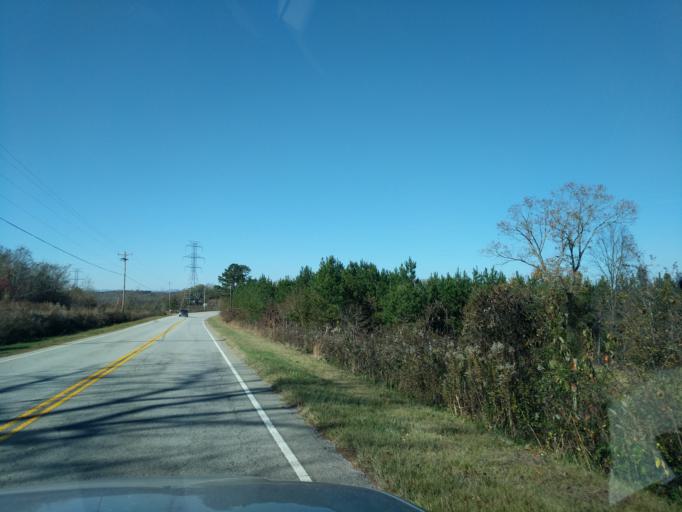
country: US
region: South Carolina
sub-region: Greenville County
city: Tigerville
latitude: 34.9984
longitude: -82.3525
